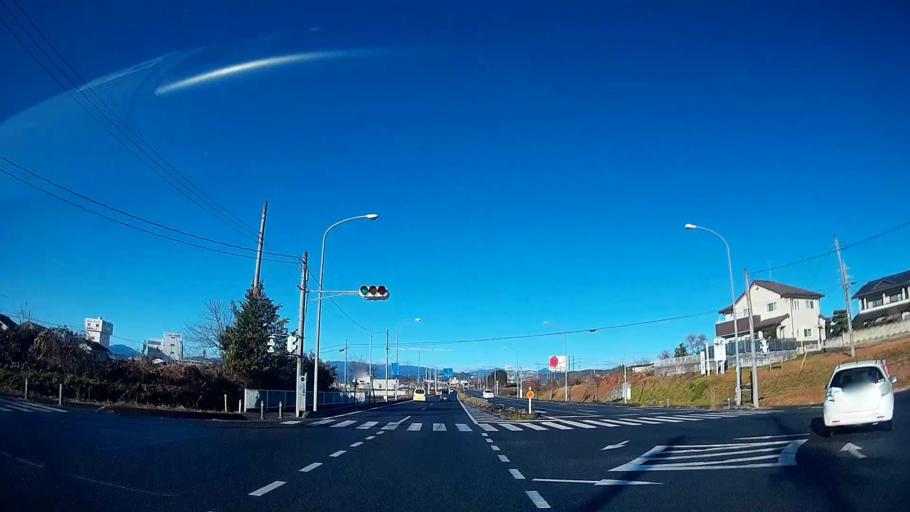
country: JP
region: Saitama
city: Hanno
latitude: 35.8578
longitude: 139.3419
